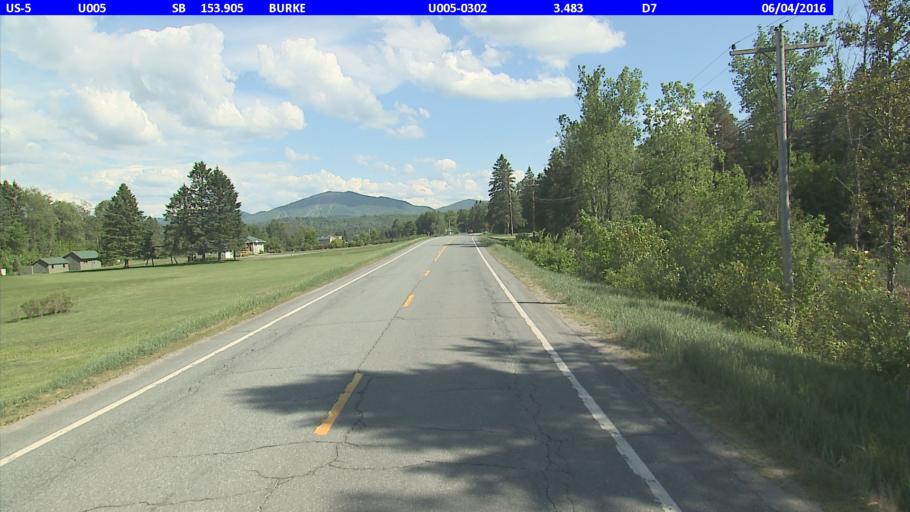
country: US
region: Vermont
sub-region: Caledonia County
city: Lyndonville
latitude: 44.6337
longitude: -71.9753
